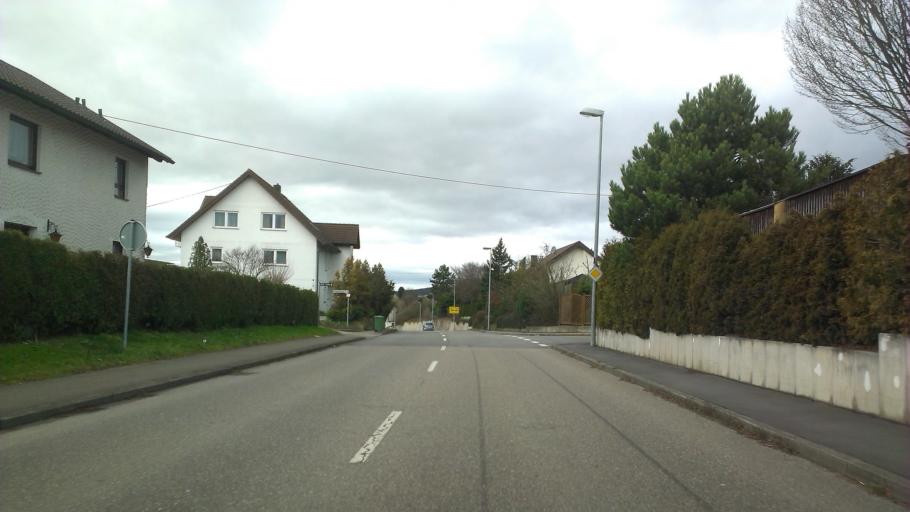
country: DE
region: Baden-Wuerttemberg
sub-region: Karlsruhe Region
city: Illingen
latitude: 48.9520
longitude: 8.9276
